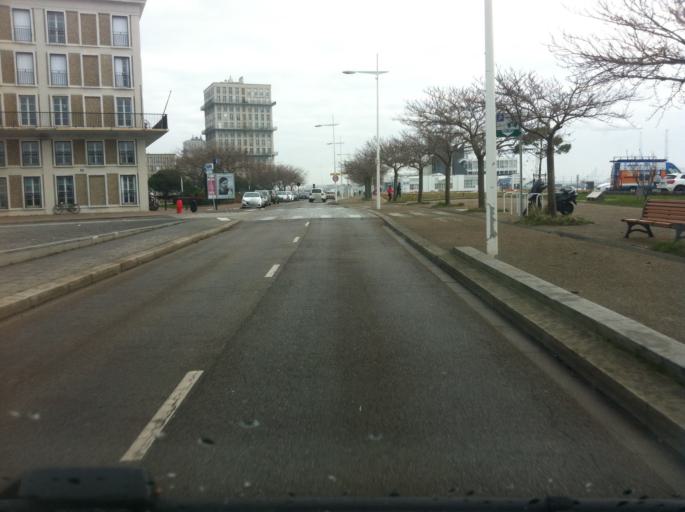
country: FR
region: Haute-Normandie
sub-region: Departement de la Seine-Maritime
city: Le Havre
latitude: 49.4845
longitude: 0.1029
